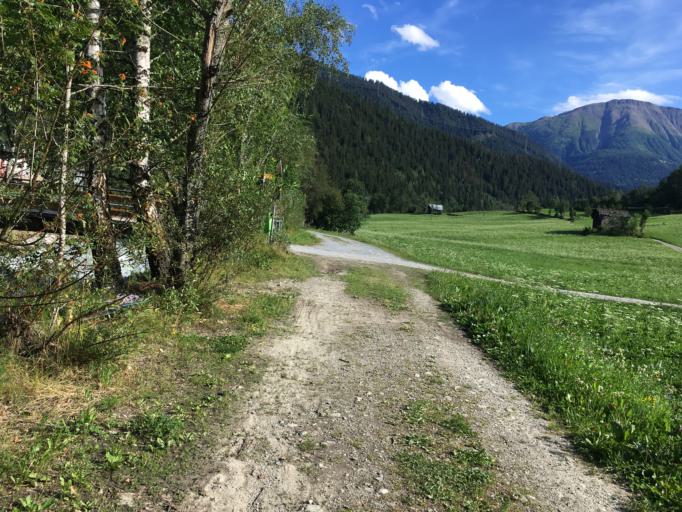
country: CH
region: Valais
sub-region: Goms District
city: Fiesch
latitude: 46.4186
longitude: 8.1408
